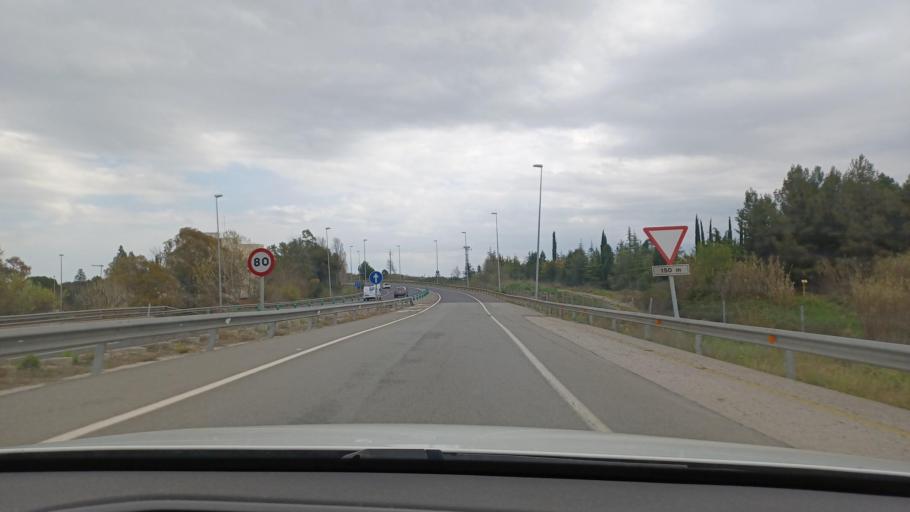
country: ES
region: Catalonia
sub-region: Provincia de Barcelona
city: Sant Cugat del Valles
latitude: 41.4914
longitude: 2.0978
